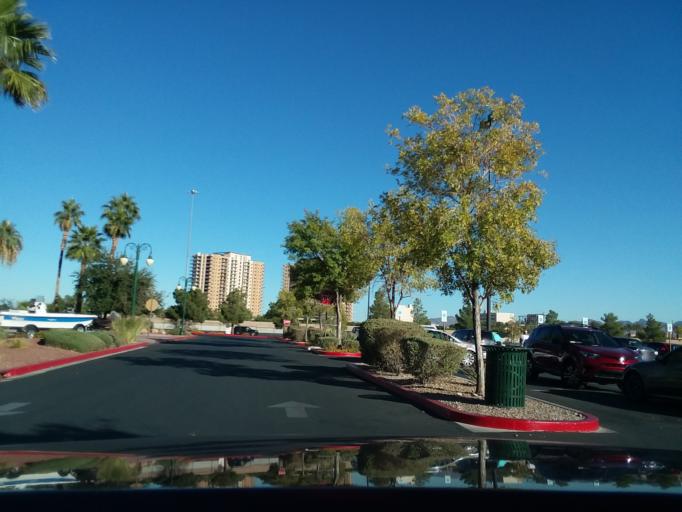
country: US
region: Nevada
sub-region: Clark County
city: Enterprise
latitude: 36.0400
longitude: -115.1823
